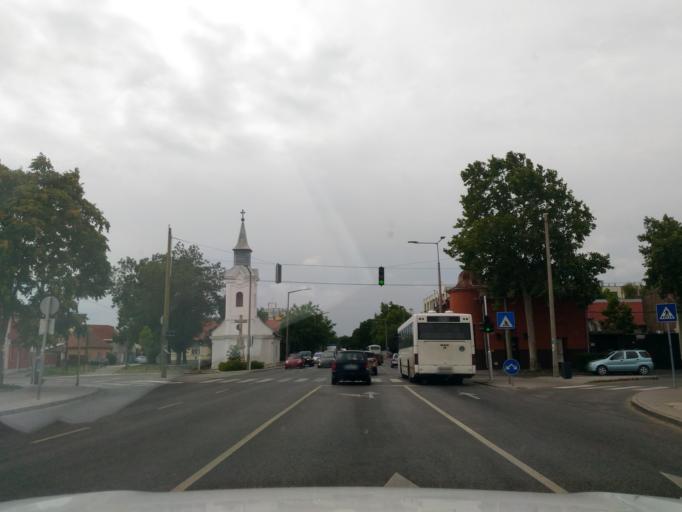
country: HU
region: Jasz-Nagykun-Szolnok
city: Szolnok
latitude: 47.1779
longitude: 20.1904
